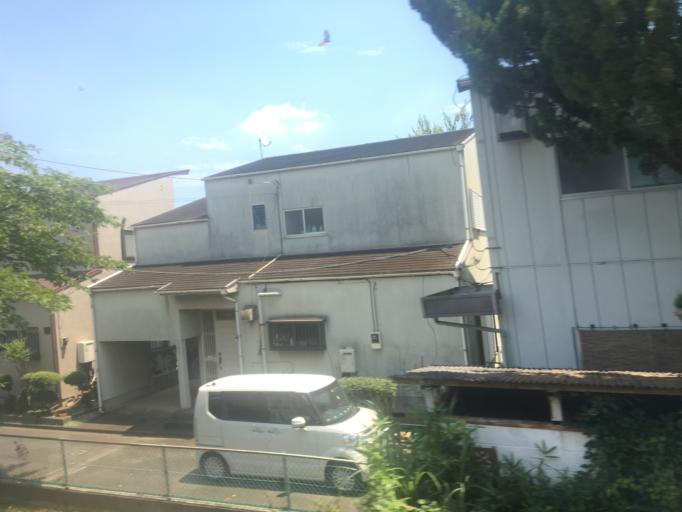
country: JP
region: Saitama
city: Yorii
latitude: 36.1277
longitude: 139.2032
